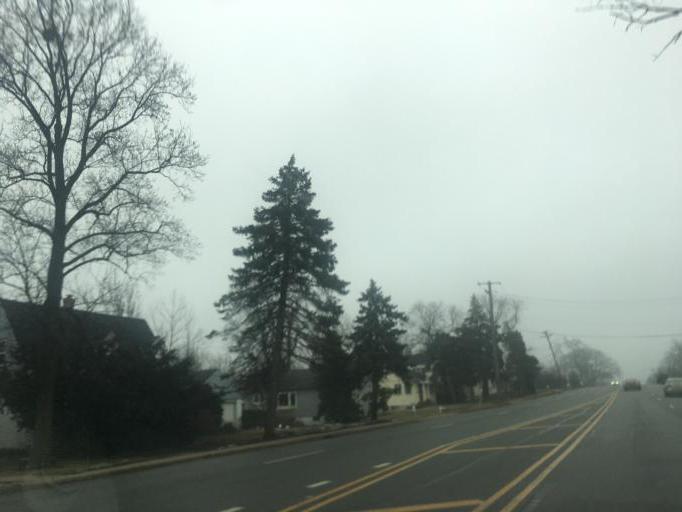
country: US
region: Illinois
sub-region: DuPage County
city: Downers Grove
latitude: 41.8054
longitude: -88.0383
